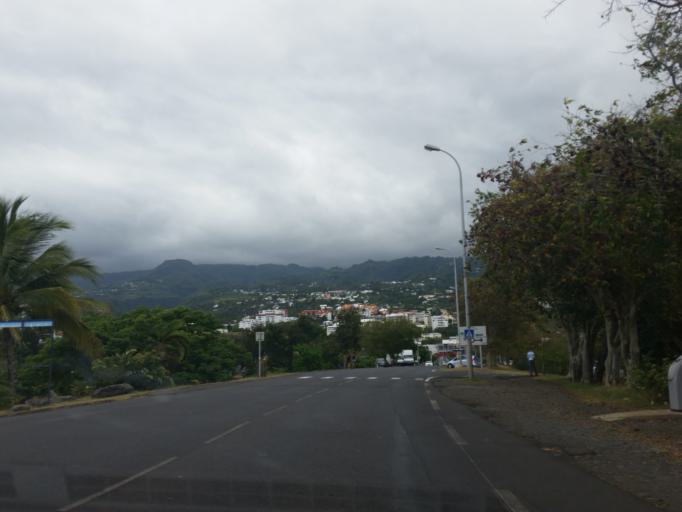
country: RE
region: Reunion
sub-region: Reunion
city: Saint-Denis
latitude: -20.8918
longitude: 55.4715
